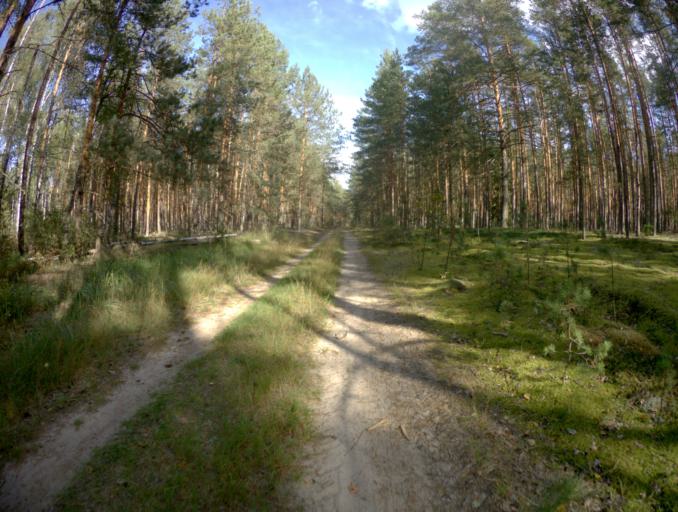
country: RU
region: Vladimir
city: Petushki
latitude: 55.8666
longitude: 39.4438
